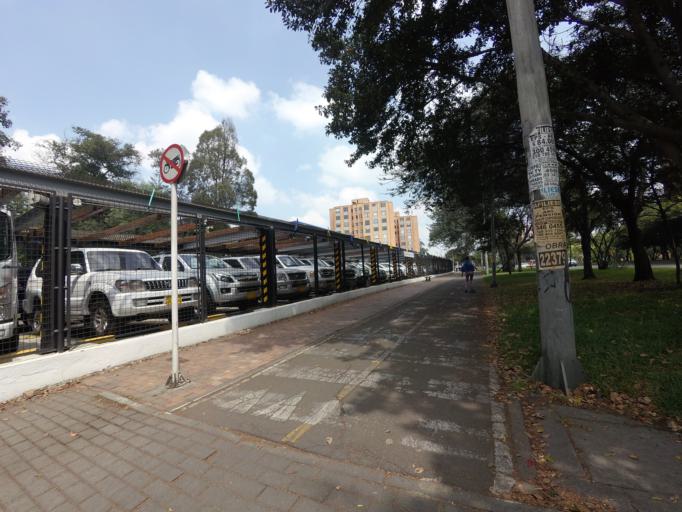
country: CO
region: Bogota D.C.
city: Barrio San Luis
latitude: 4.7170
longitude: -74.0760
